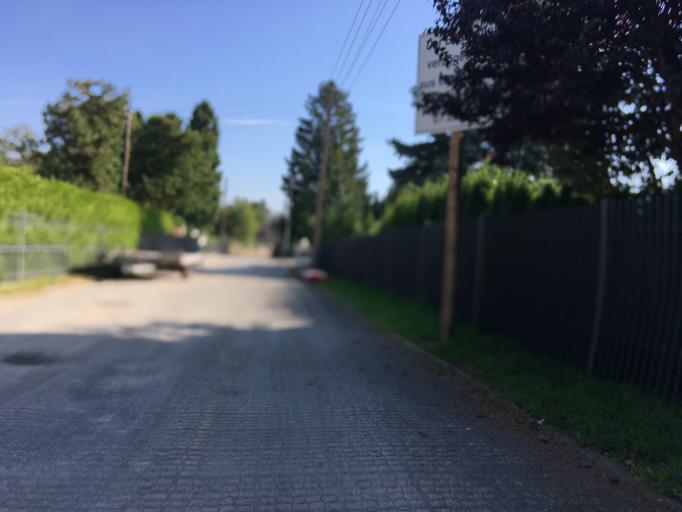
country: DE
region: Berlin
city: Rahnsdorf
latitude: 52.4320
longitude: 13.7052
